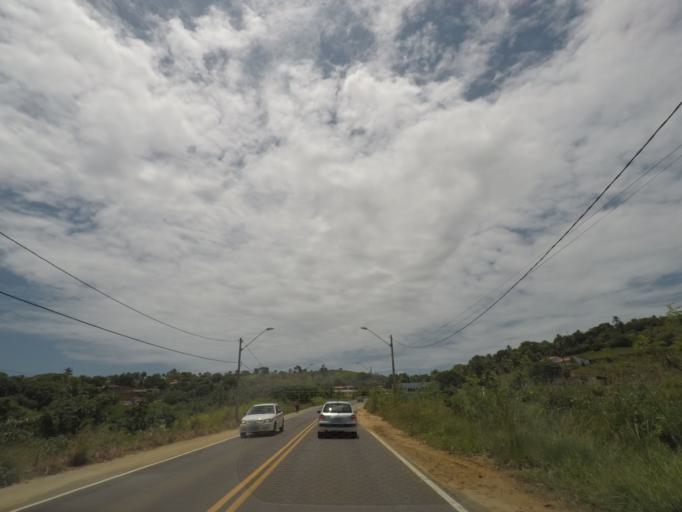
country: BR
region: Bahia
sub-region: Itaparica
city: Itaparica
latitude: -12.9362
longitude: -38.6250
